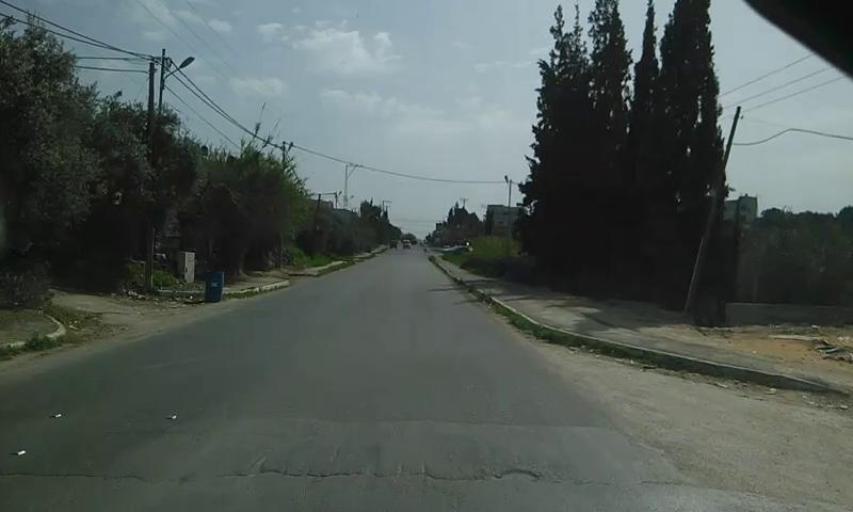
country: PS
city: Bir al Basha
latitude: 32.4218
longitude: 35.2315
